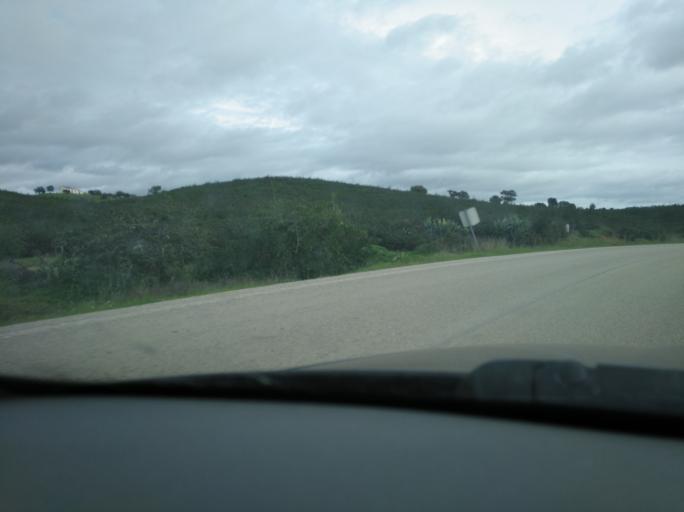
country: PT
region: Faro
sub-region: Castro Marim
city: Castro Marim
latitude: 37.2200
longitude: -7.4701
